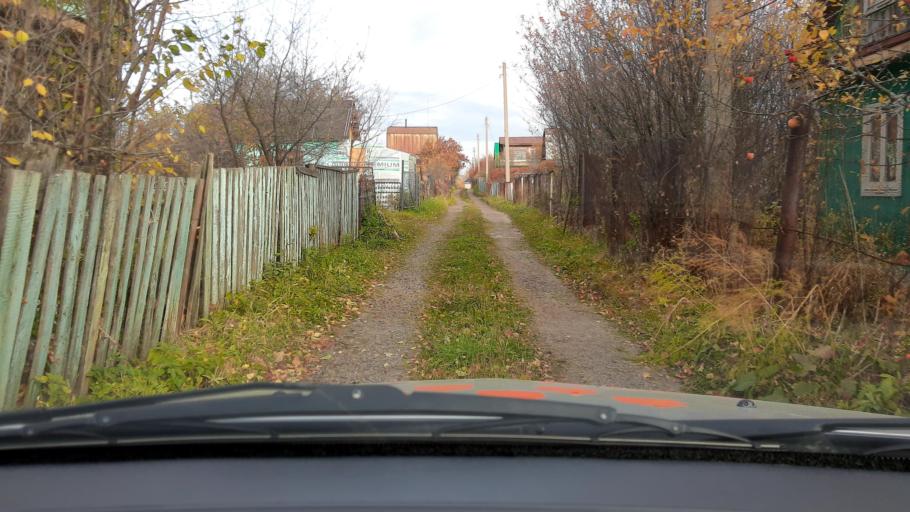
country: RU
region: Bashkortostan
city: Asanovo
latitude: 54.8045
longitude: 55.6128
